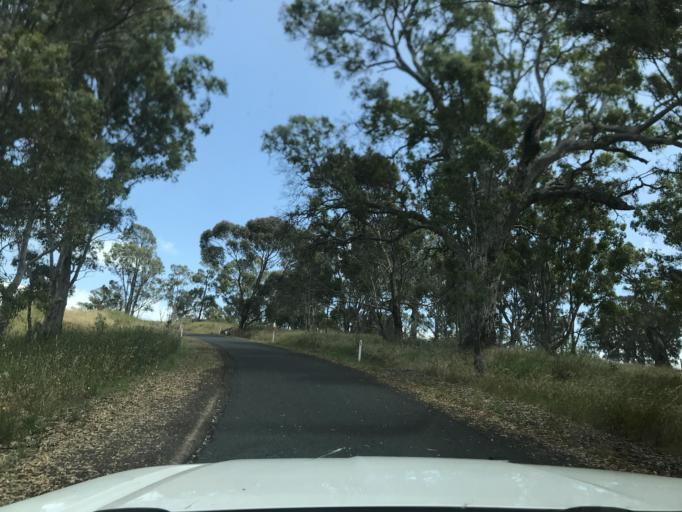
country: AU
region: South Australia
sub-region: Wattle Range
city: Penola
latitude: -37.2670
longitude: 141.5119
